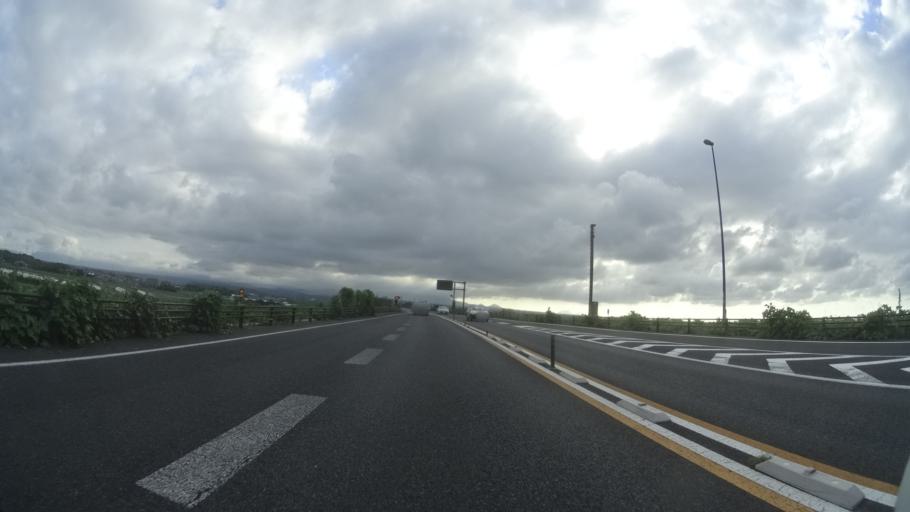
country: JP
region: Tottori
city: Kurayoshi
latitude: 35.4984
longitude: 133.7154
